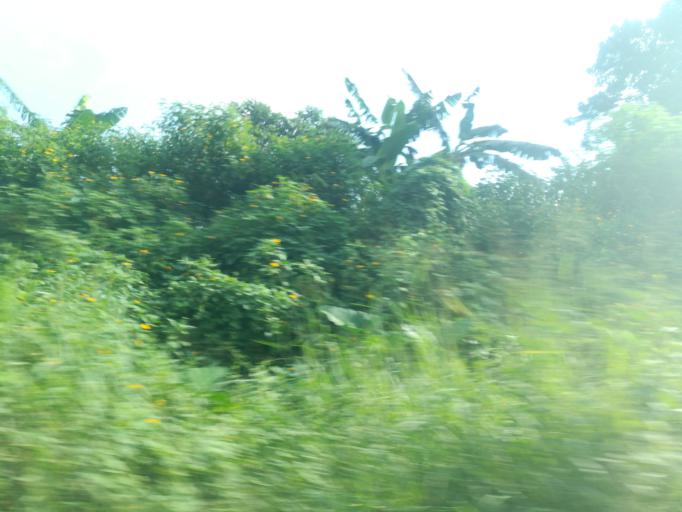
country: NG
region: Oyo
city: Ido
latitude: 7.3960
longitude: 3.7881
